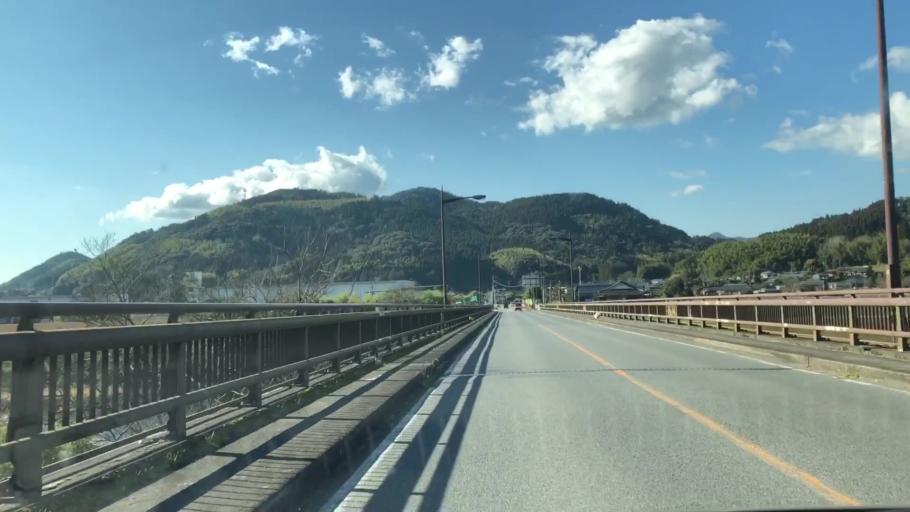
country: JP
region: Kagoshima
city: Satsumasendai
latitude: 31.8680
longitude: 130.4310
